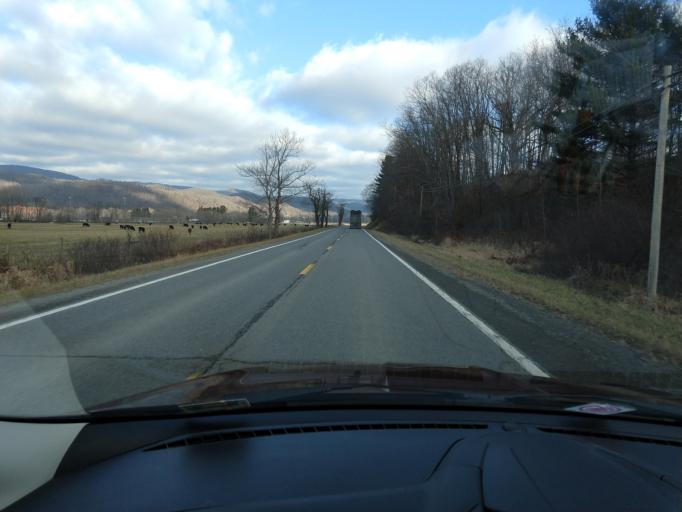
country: US
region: West Virginia
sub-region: Randolph County
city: Elkins
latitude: 38.6888
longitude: -79.9740
